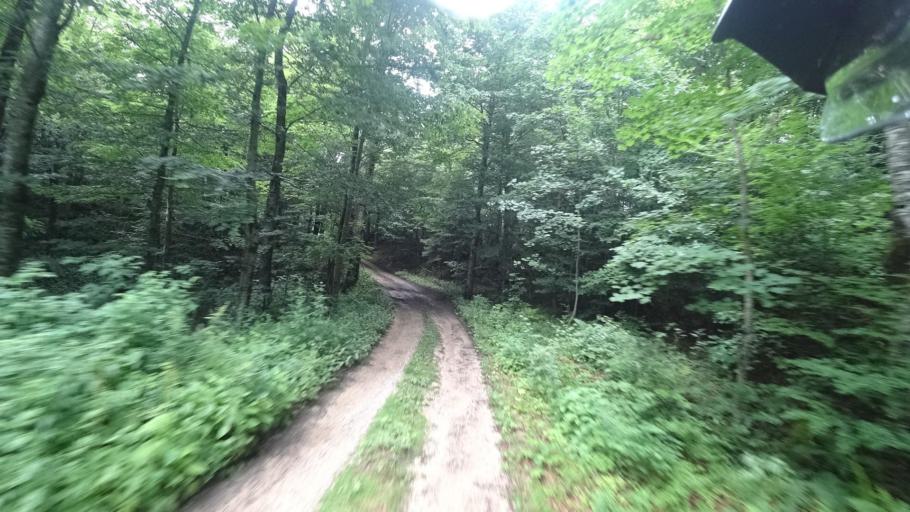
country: HR
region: Licko-Senjska
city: Jezerce
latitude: 44.7847
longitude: 15.6434
